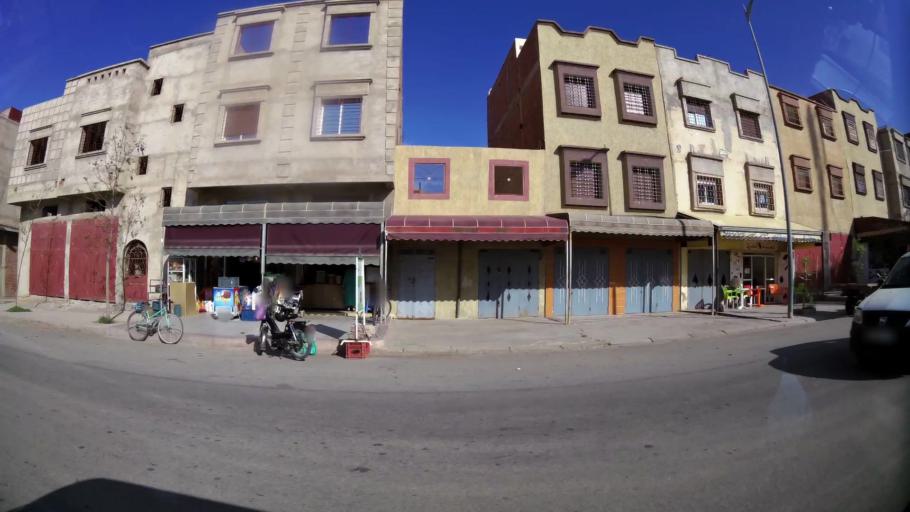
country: MA
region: Oriental
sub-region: Oujda-Angad
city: Oujda
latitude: 34.7156
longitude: -1.8922
